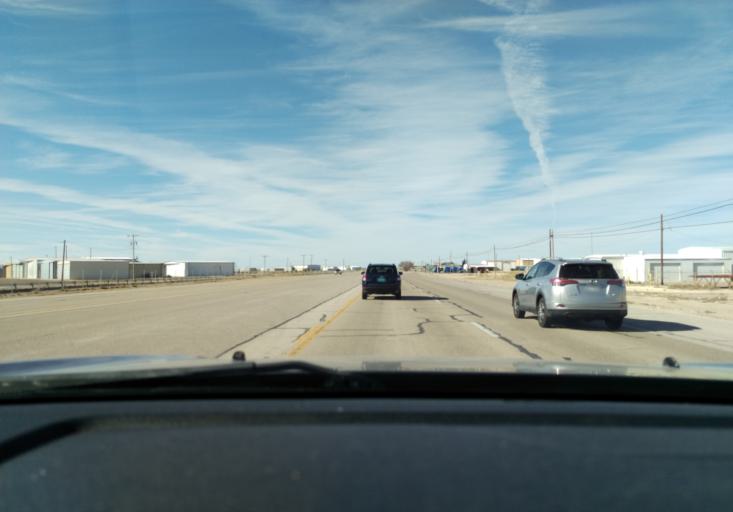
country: US
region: New Mexico
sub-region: Lea County
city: Hobbs
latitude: 32.6967
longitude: -103.2079
